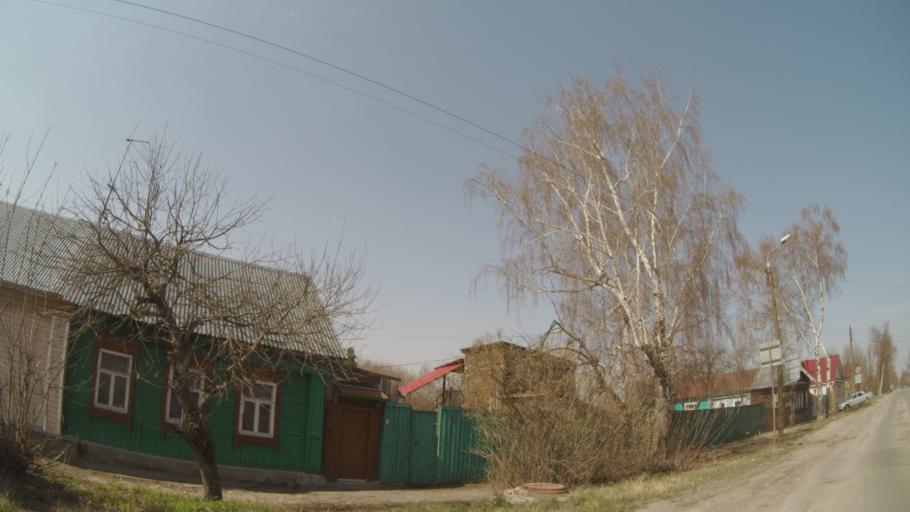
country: RU
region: Nizjnij Novgorod
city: Arzamas
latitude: 55.3869
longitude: 43.8237
